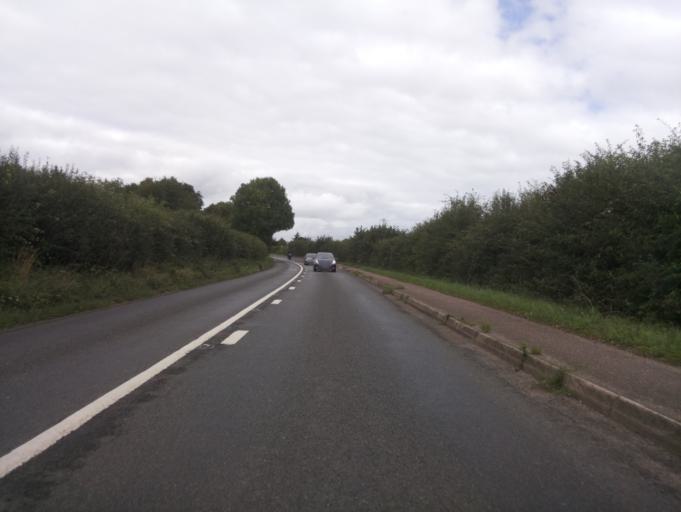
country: GB
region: England
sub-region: Devon
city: Cullompton
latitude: 50.8732
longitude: -3.3870
